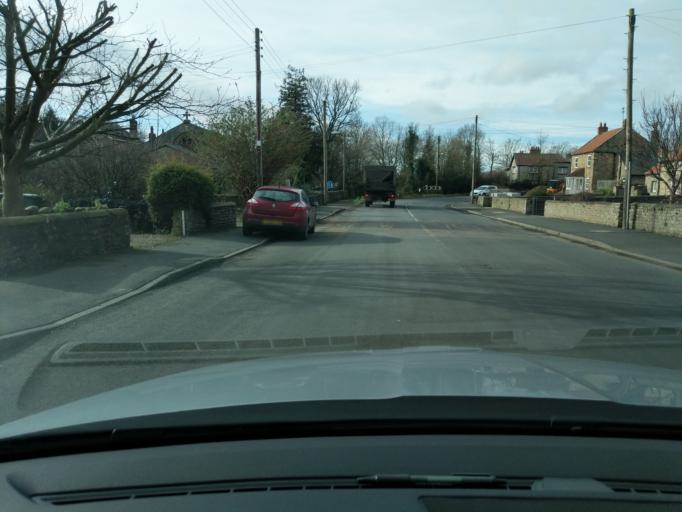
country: GB
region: England
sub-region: North Yorkshire
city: Catterick
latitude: 54.3924
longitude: -1.6686
